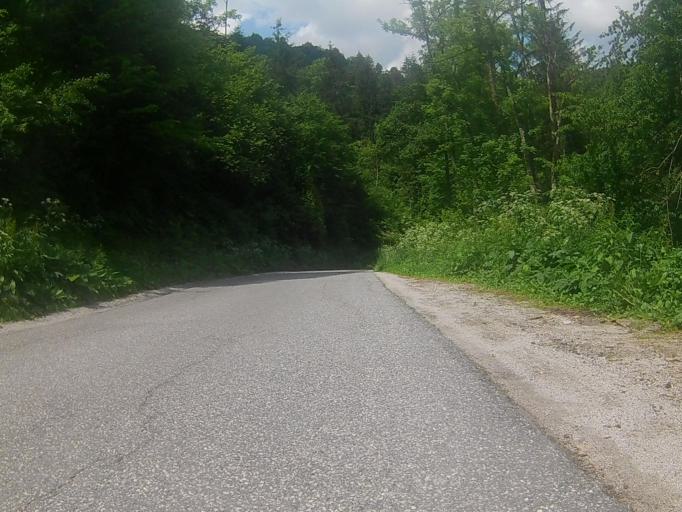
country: SI
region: Maribor
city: Bresternica
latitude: 46.5790
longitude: 15.5667
